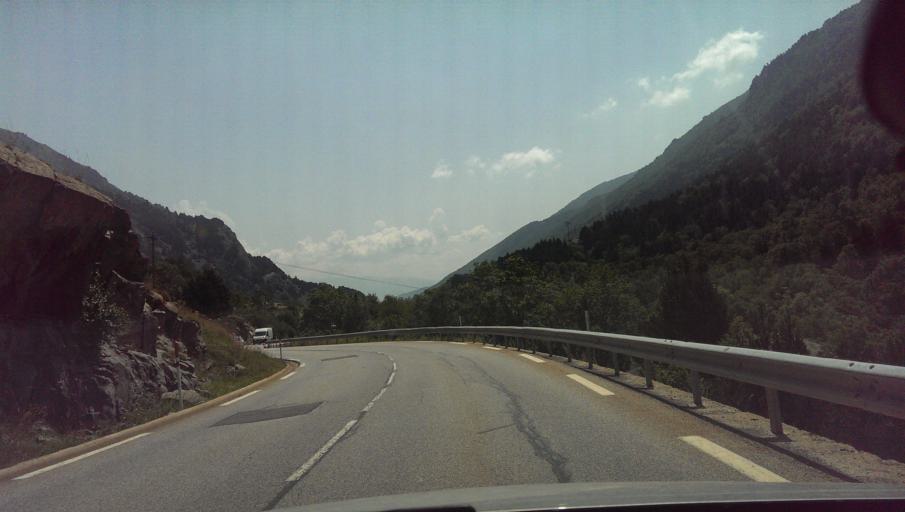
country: ES
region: Catalonia
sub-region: Provincia de Girona
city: Meranges
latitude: 42.5138
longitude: 1.8246
